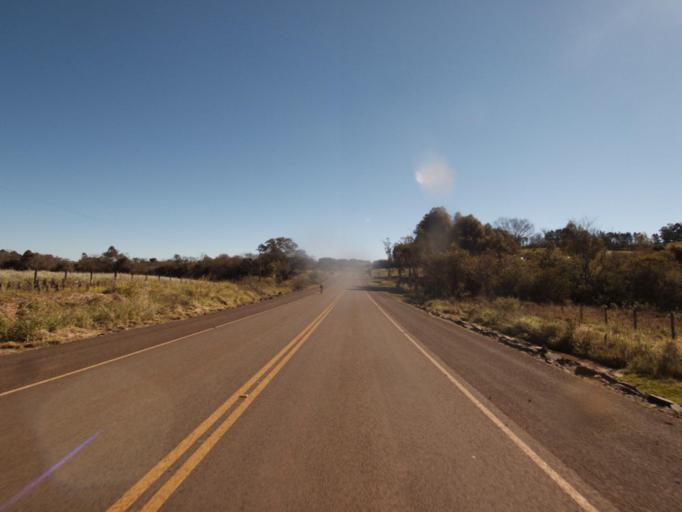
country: AR
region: Misiones
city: Bernardo de Irigoyen
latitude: -26.6138
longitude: -53.6760
